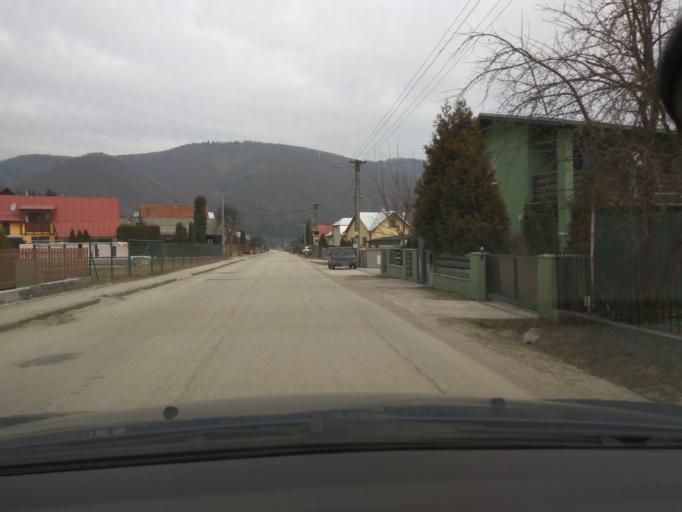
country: SK
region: Zilinsky
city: Rajec
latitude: 49.1195
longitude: 18.6736
